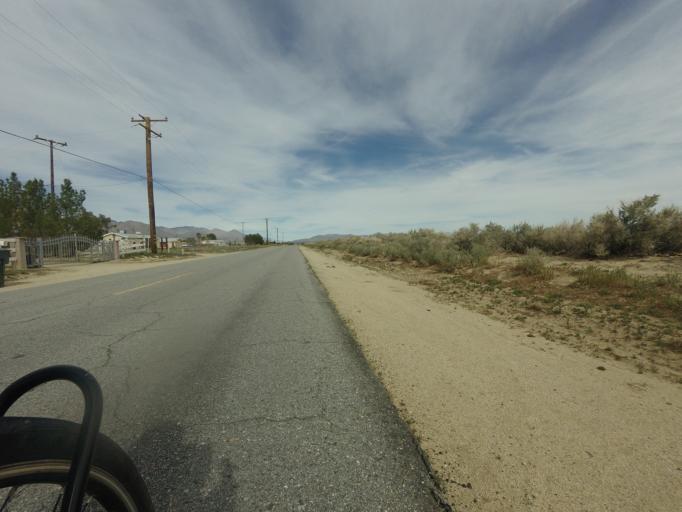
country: US
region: California
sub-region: Kern County
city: Inyokern
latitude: 35.7521
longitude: -117.8436
